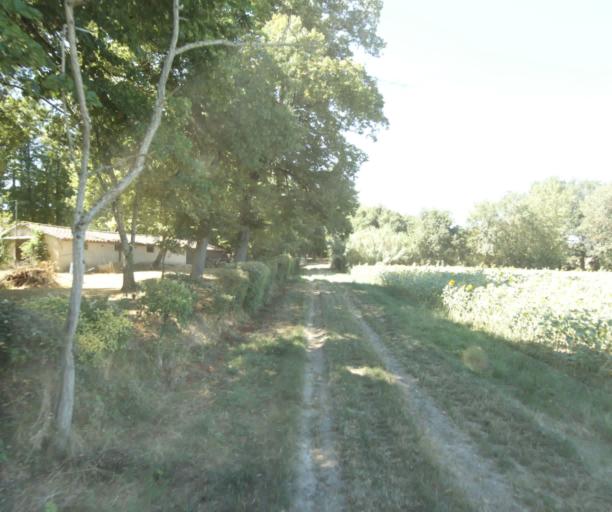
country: FR
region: Midi-Pyrenees
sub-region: Departement de la Haute-Garonne
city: Saint-Felix-Lauragais
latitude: 43.4825
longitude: 1.9243
